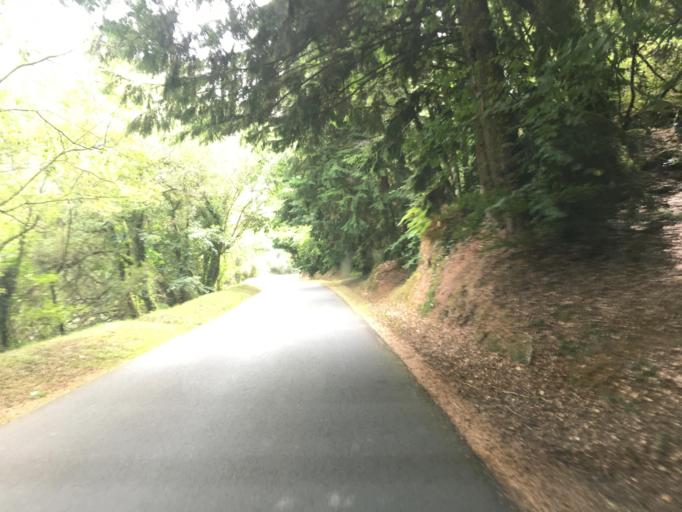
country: FR
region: Brittany
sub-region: Departement des Cotes-d'Armor
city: Gouarec
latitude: 48.2081
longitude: -3.1167
